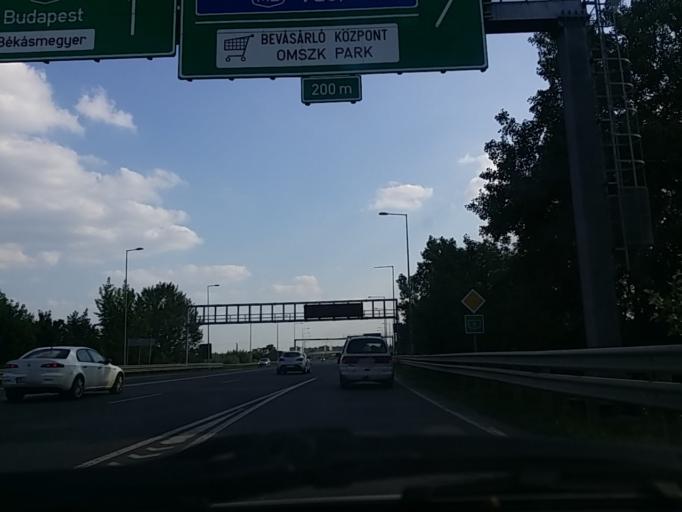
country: HU
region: Pest
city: Budakalasz
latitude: 47.6180
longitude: 19.0658
